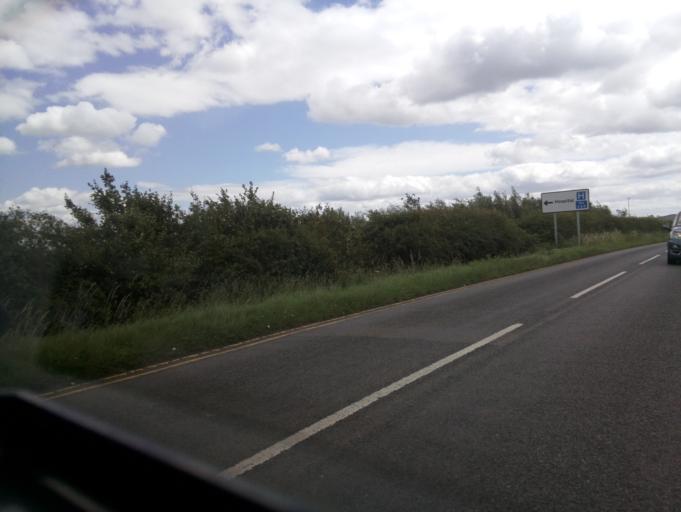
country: GB
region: England
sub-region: Nottinghamshire
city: West Bridgford
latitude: 52.9193
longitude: -1.0876
